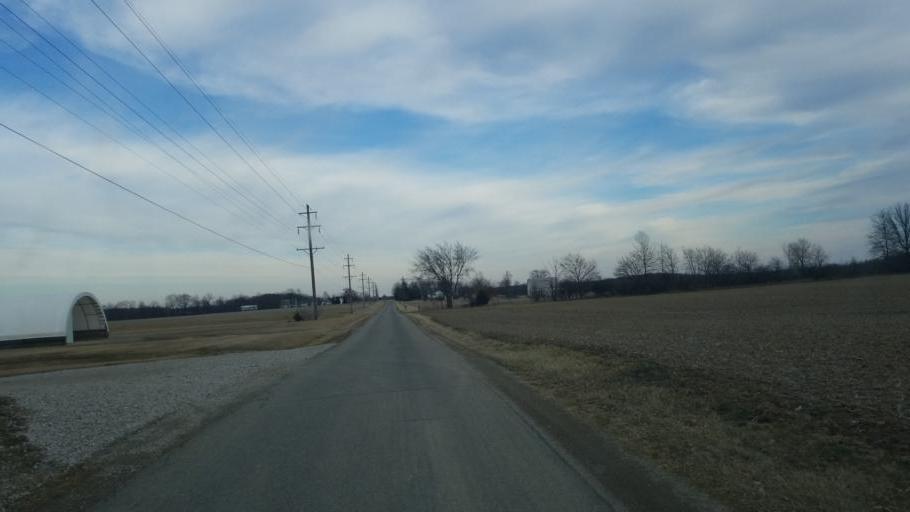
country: US
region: Ohio
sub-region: Defiance County
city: Hicksville
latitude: 41.3536
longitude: -84.7640
